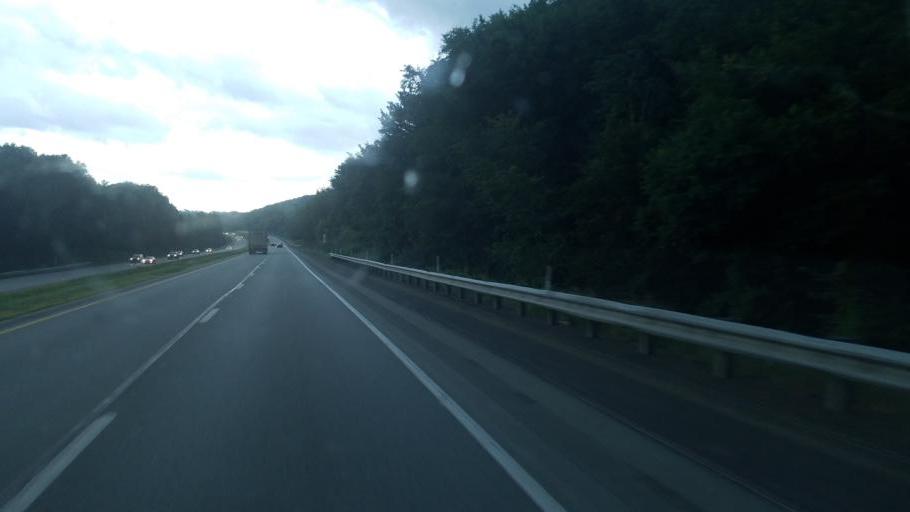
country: US
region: Pennsylvania
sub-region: Butler County
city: Zelienople
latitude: 40.8650
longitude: -80.1107
